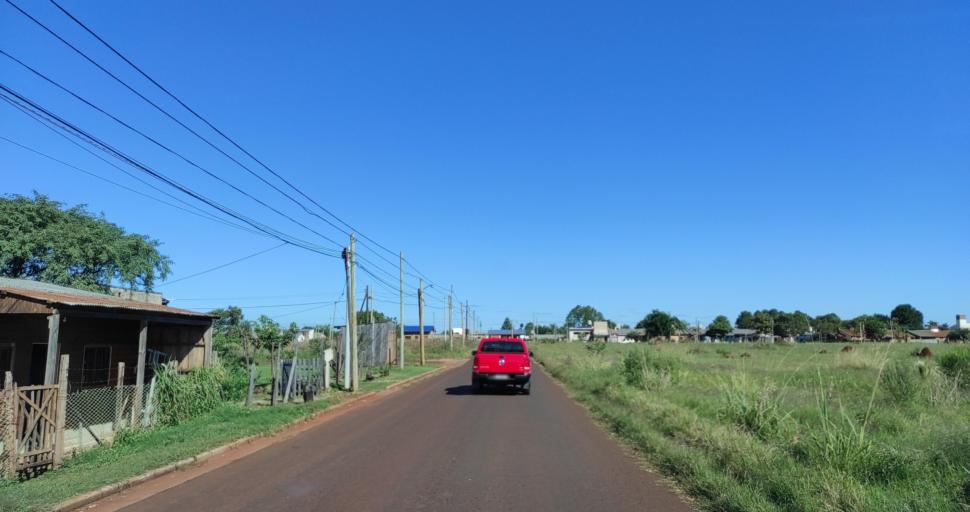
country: AR
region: Misiones
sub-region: Departamento de Capital
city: Posadas
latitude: -27.4280
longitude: -55.9297
